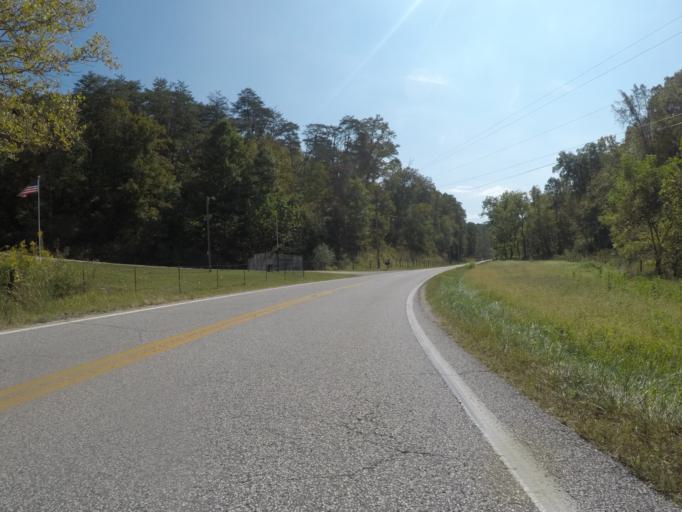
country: US
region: West Virginia
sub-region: Cabell County
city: Lesage
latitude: 38.5786
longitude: -82.4108
